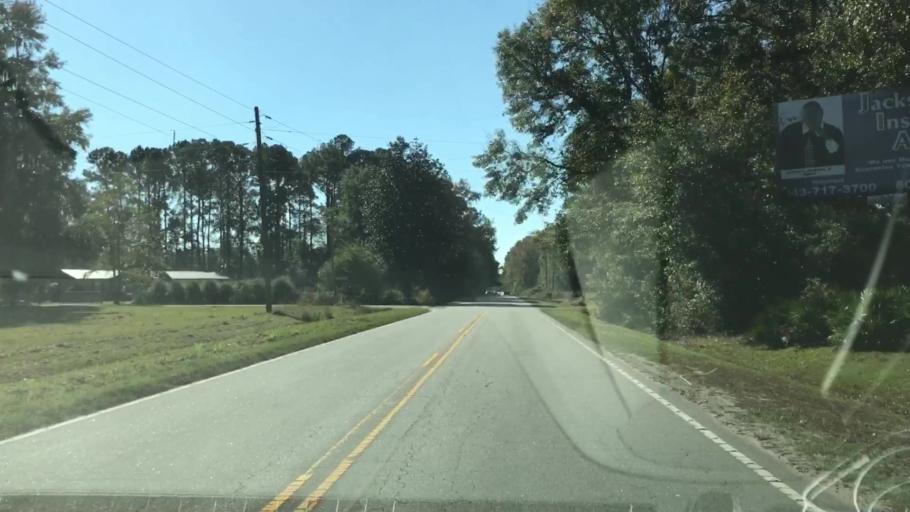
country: US
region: South Carolina
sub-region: Jasper County
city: Ridgeland
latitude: 32.4294
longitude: -80.8960
